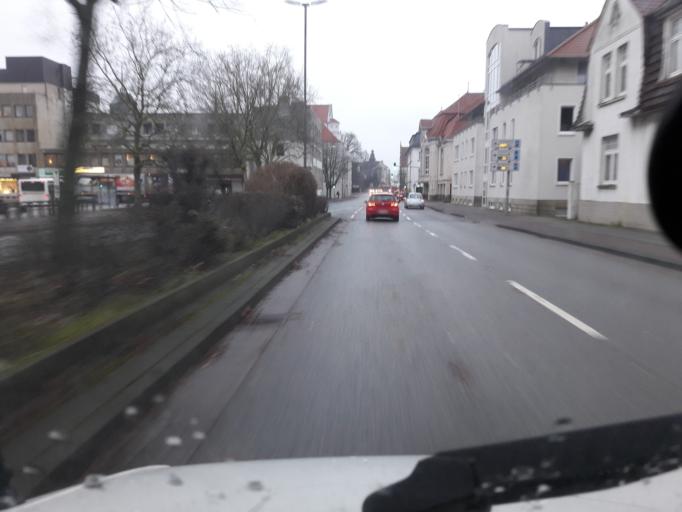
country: DE
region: North Rhine-Westphalia
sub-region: Regierungsbezirk Detmold
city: Minden
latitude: 52.2865
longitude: 8.9179
